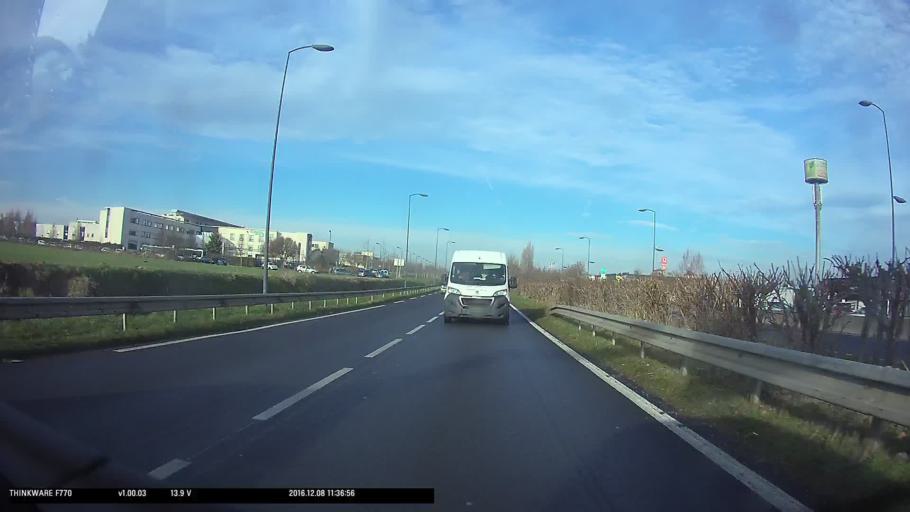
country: FR
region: Ile-de-France
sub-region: Departement du Val-d'Oise
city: Osny
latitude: 49.0735
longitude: 2.0788
